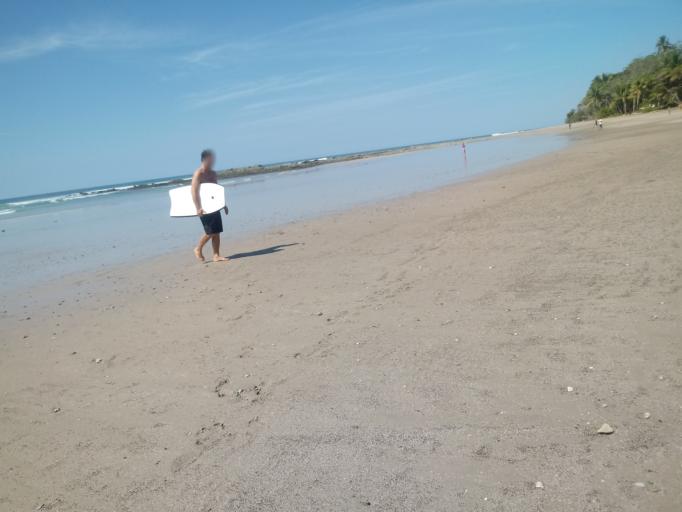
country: CR
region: Guanacaste
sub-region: Canton de Nandayure
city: Bejuco
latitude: 9.6681
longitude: -85.1944
